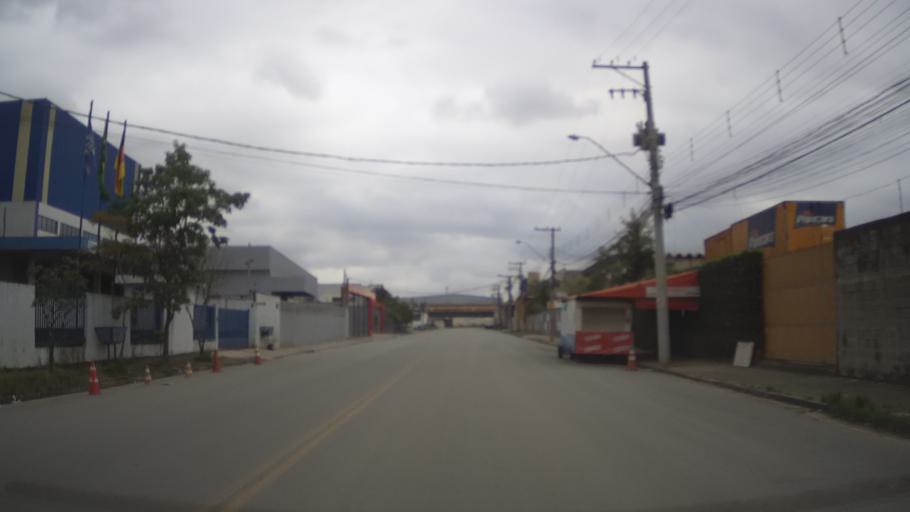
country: BR
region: Sao Paulo
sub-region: Guarulhos
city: Guarulhos
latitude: -23.4341
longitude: -46.4999
